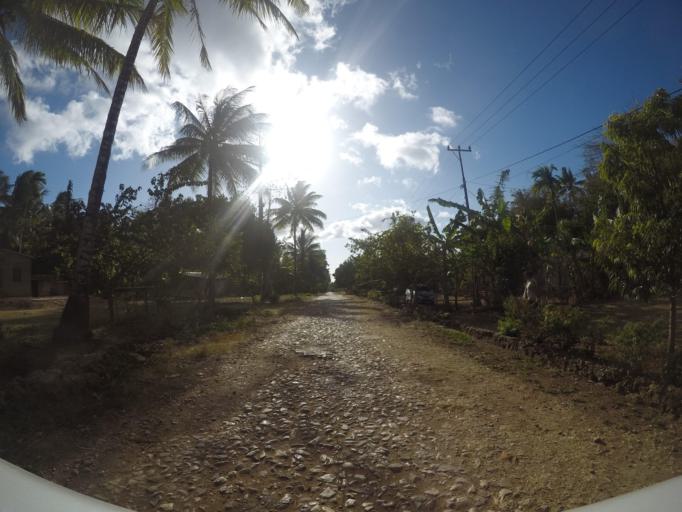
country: TL
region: Lautem
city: Lospalos
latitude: -8.4460
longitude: 126.8747
